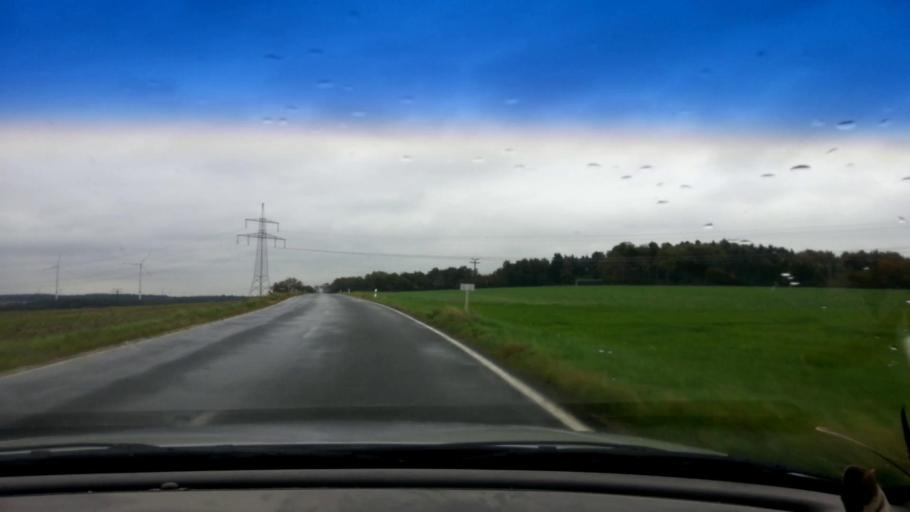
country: DE
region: Bavaria
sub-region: Upper Franconia
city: Poxdorf
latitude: 49.9647
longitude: 11.1025
